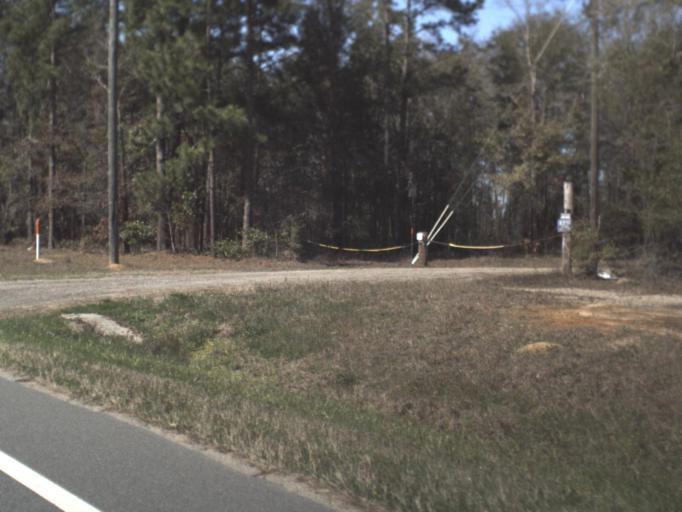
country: US
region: Florida
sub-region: Gadsden County
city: Chattahoochee
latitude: 30.6953
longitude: -84.7607
